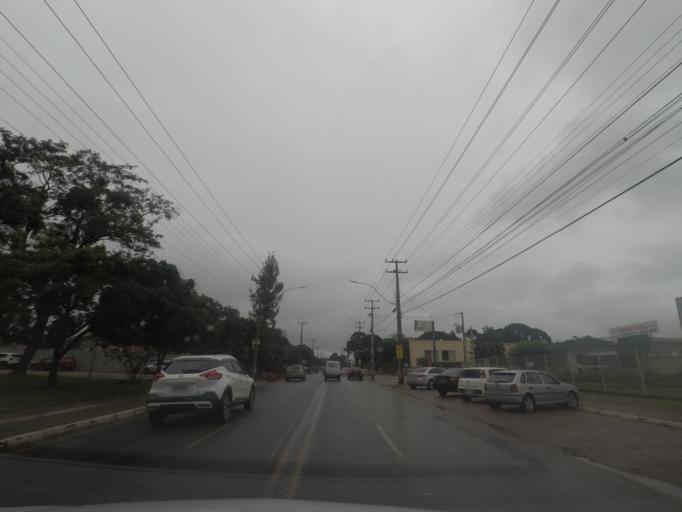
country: BR
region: Parana
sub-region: Piraquara
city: Piraquara
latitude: -25.4510
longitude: -49.0697
